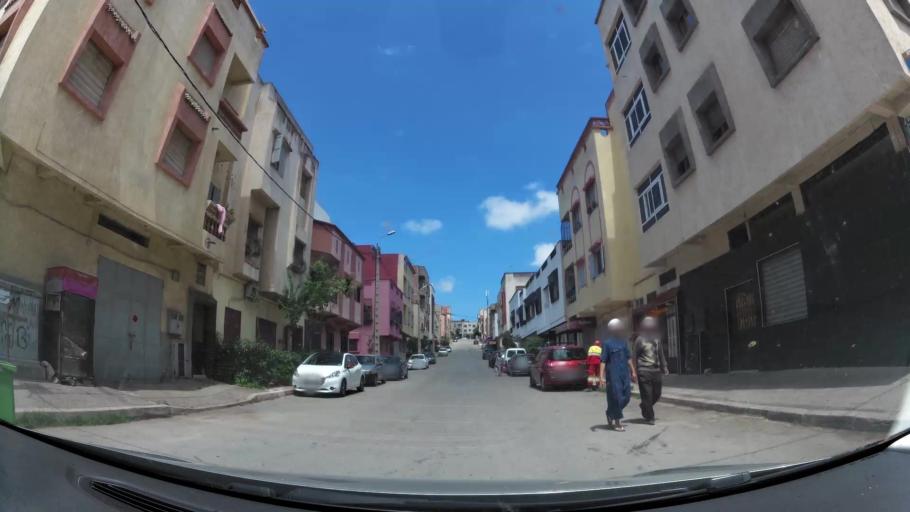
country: MA
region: Gharb-Chrarda-Beni Hssen
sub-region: Kenitra Province
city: Kenitra
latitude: 34.2729
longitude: -6.5995
